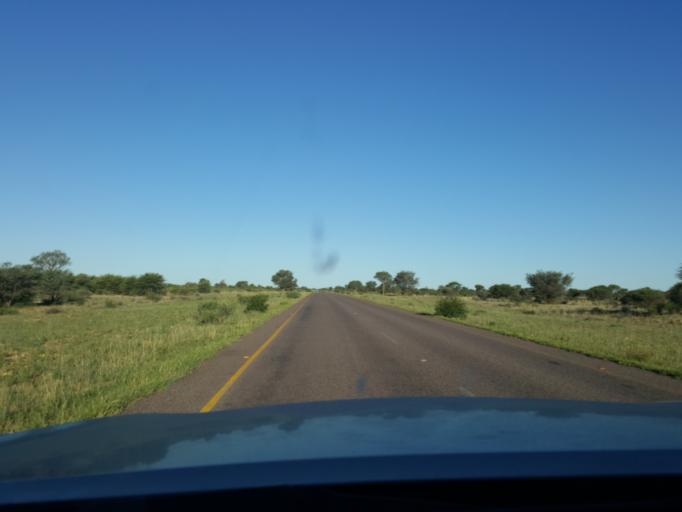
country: BW
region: Southern
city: Khakhea
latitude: -24.3089
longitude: 23.4100
